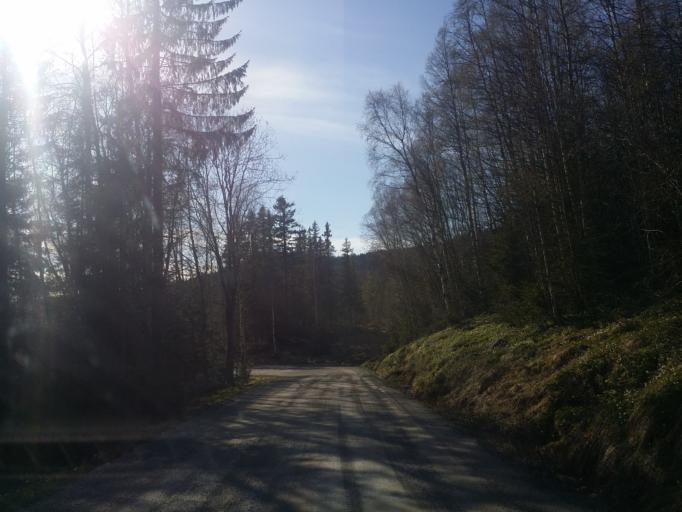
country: NO
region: Telemark
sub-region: Seljord
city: Seljord
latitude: 59.6204
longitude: 8.6881
